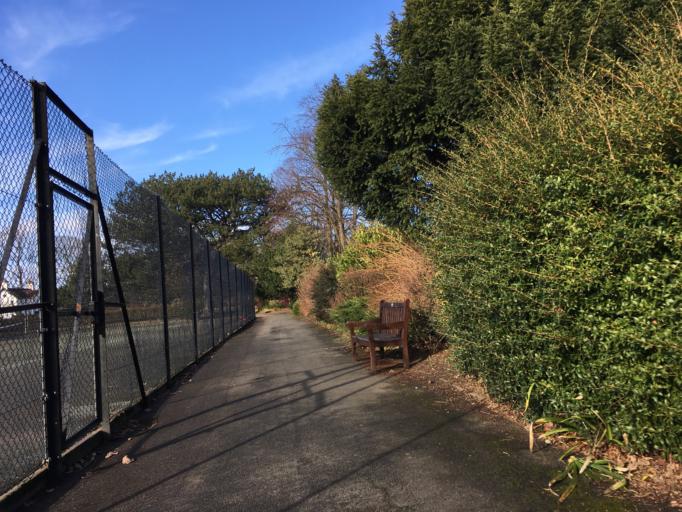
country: GB
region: England
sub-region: Cheshire West and Chester
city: Hoole
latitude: 53.2012
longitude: -2.8688
